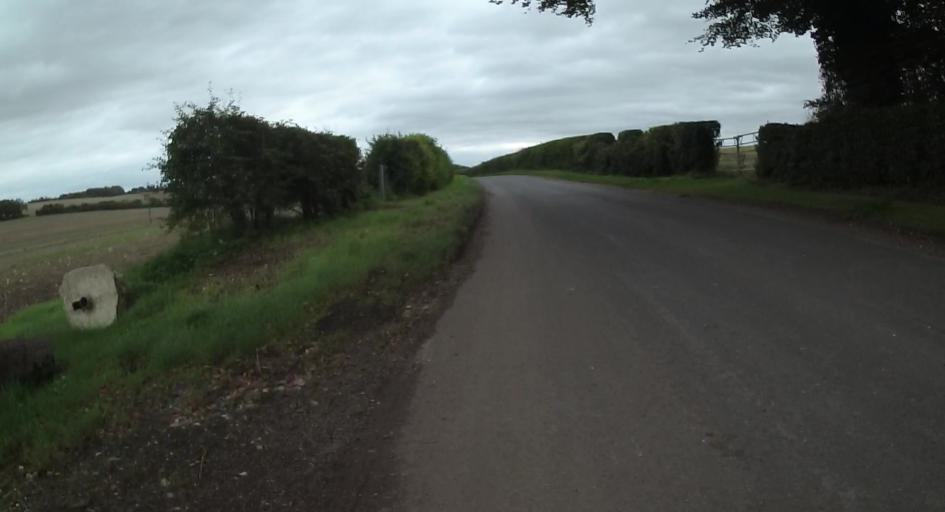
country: GB
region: England
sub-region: Hampshire
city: Four Marks
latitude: 51.1633
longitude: -1.1274
